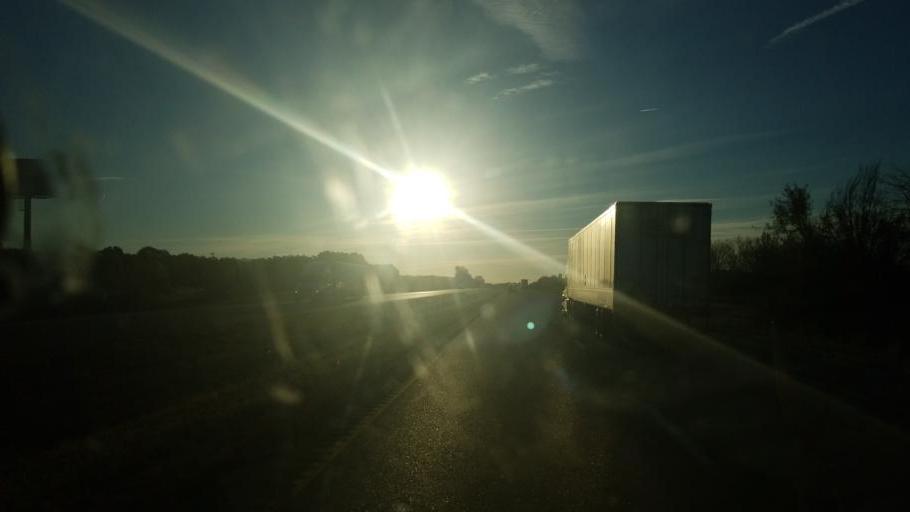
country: US
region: Missouri
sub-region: Montgomery County
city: Montgomery City
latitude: 38.9007
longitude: -91.6383
